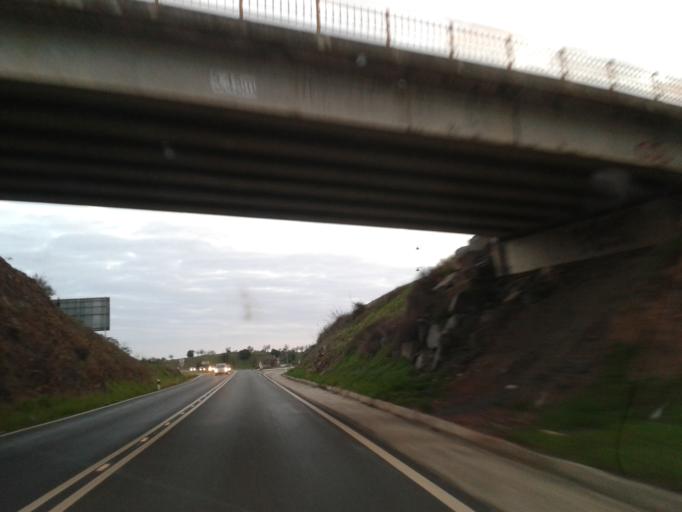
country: PT
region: Faro
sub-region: Castro Marim
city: Castro Marim
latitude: 37.2167
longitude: -7.4383
